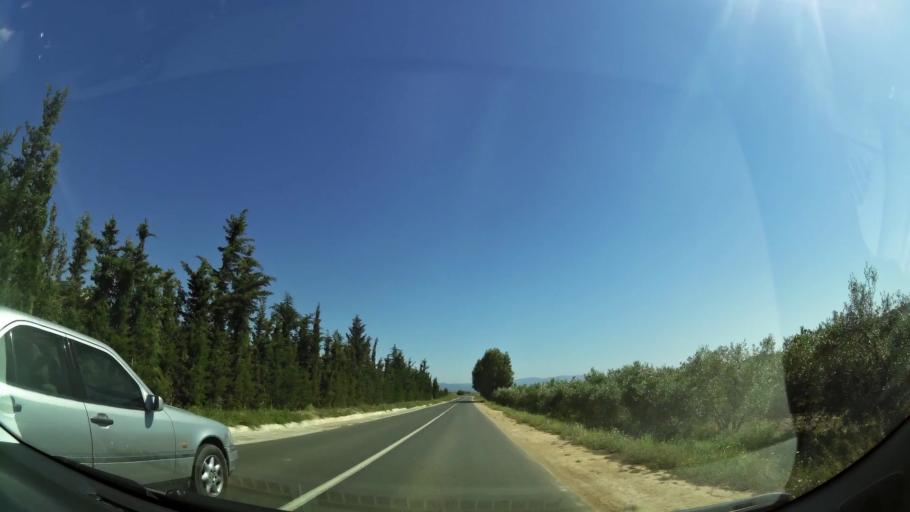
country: MA
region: Oriental
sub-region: Berkane-Taourirt
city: Madagh
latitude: 35.0472
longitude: -2.4292
